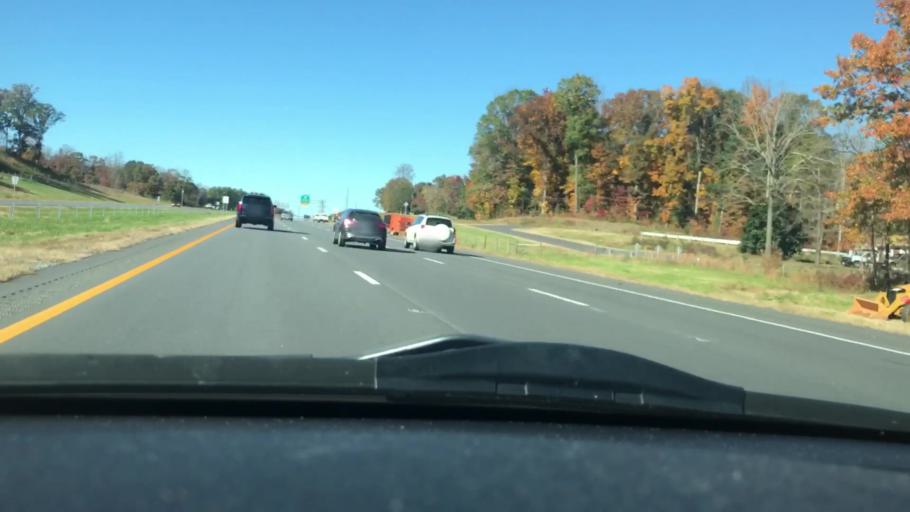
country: US
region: North Carolina
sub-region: Guilford County
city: Summerfield
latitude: 36.2327
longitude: -79.9161
